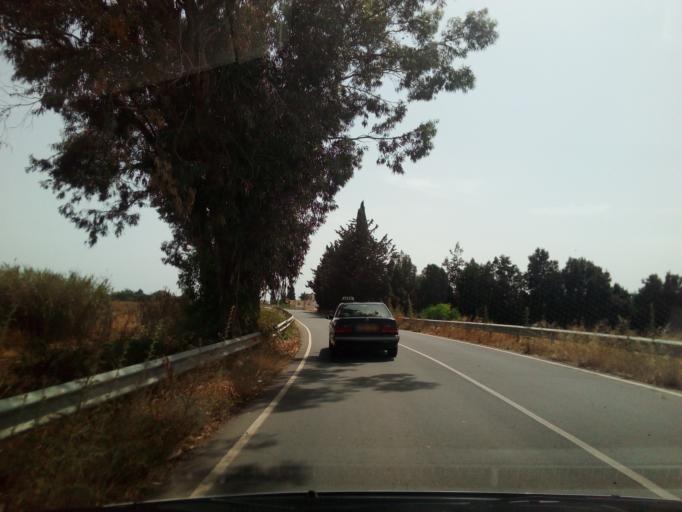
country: CY
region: Larnaka
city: Perivolia
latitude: 34.8382
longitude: 33.5887
